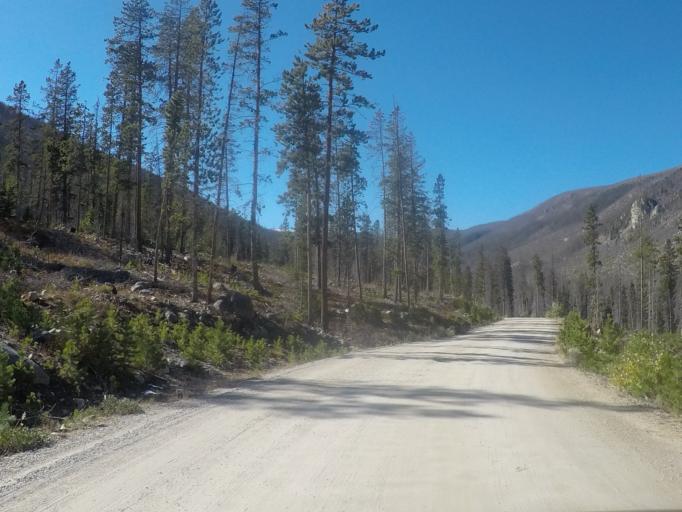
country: US
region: Montana
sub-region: Carbon County
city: Red Lodge
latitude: 45.1690
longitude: -109.4159
